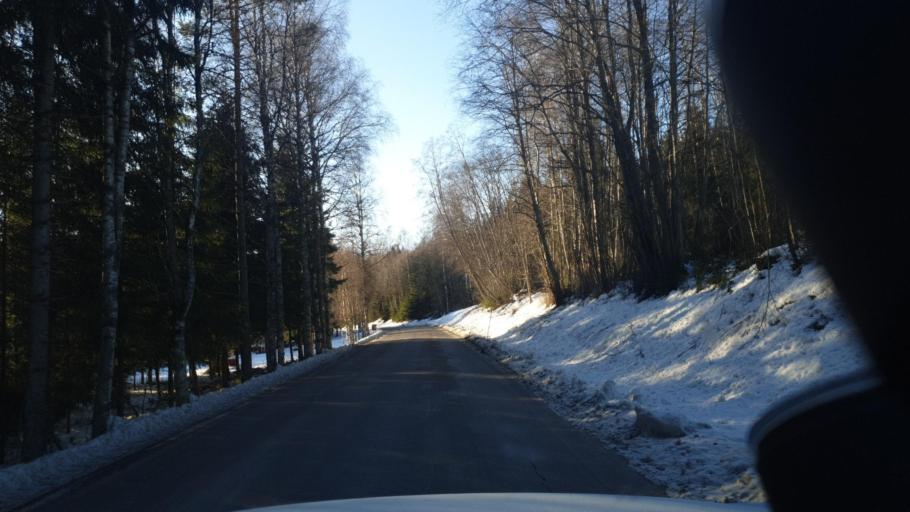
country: SE
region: Vaermland
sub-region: Arvika Kommun
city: Arvika
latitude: 59.7177
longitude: 12.7969
